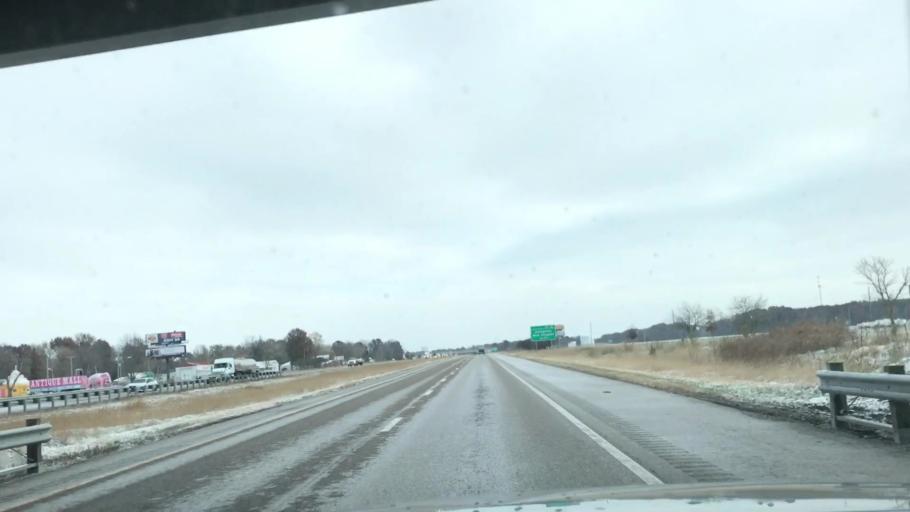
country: US
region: Illinois
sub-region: Macoupin County
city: Staunton
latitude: 38.9584
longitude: -89.7652
